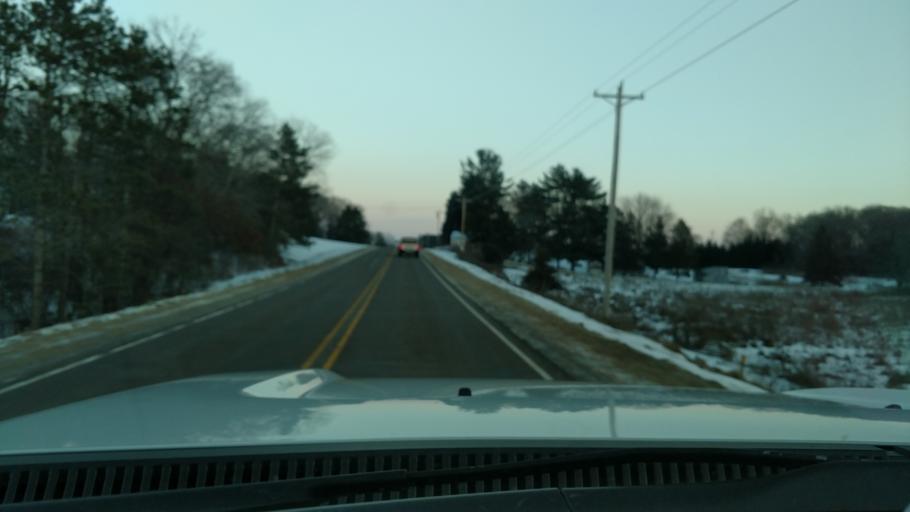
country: US
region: Wisconsin
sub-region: Saint Croix County
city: Roberts
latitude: 44.9133
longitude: -92.5140
